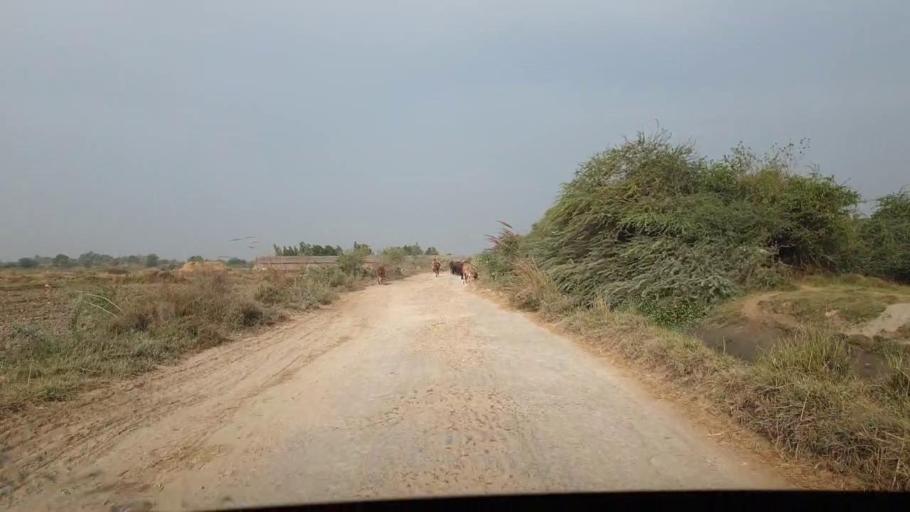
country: PK
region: Sindh
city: Chuhar Jamali
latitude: 24.3917
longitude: 67.9760
